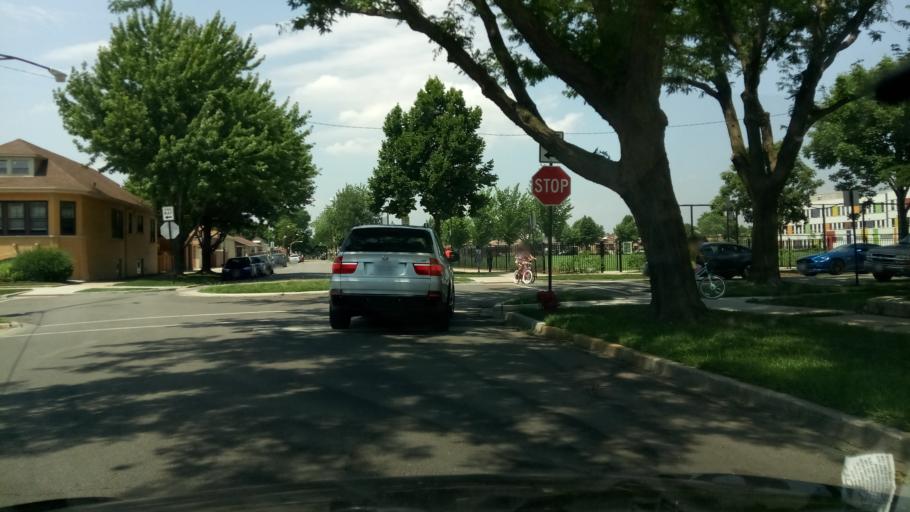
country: US
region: Illinois
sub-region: Cook County
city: Hometown
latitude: 41.7823
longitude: -87.7243
